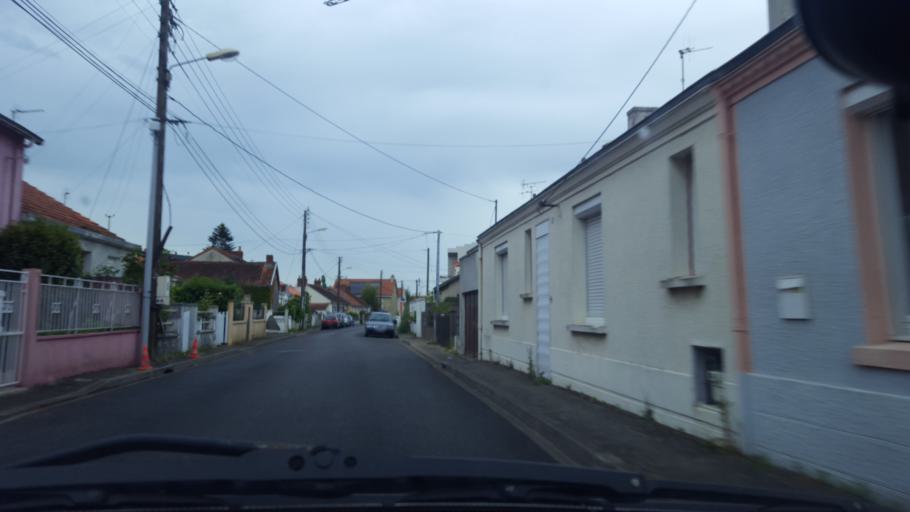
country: FR
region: Pays de la Loire
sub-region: Departement de la Loire-Atlantique
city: Reze
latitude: 47.1803
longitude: -1.5477
